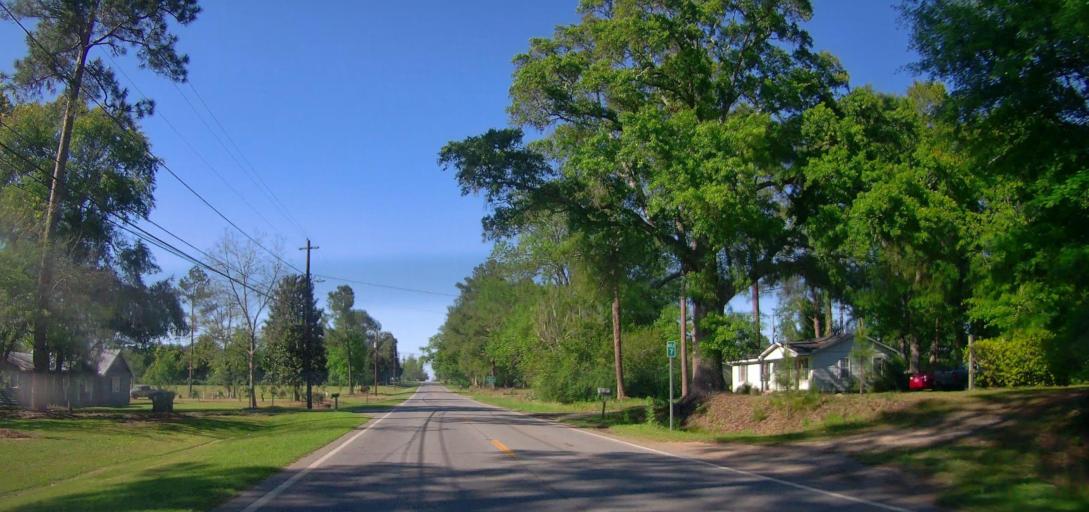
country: US
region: Georgia
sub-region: Wilcox County
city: Rochelle
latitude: 31.9401
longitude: -83.4564
